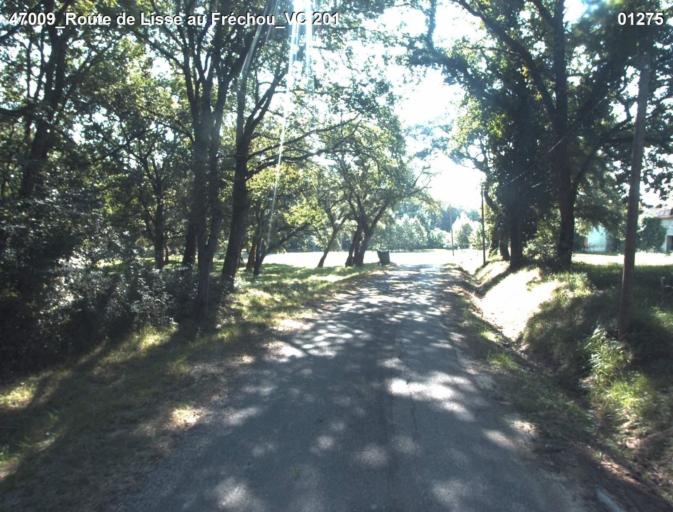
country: FR
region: Aquitaine
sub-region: Departement du Lot-et-Garonne
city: Mezin
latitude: 44.0917
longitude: 0.2960
